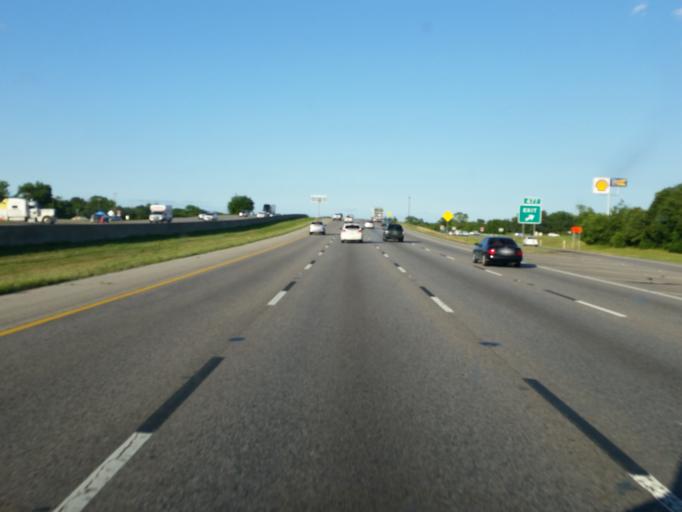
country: US
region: Texas
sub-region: Dallas County
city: Balch Springs
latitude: 32.6820
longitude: -96.6607
